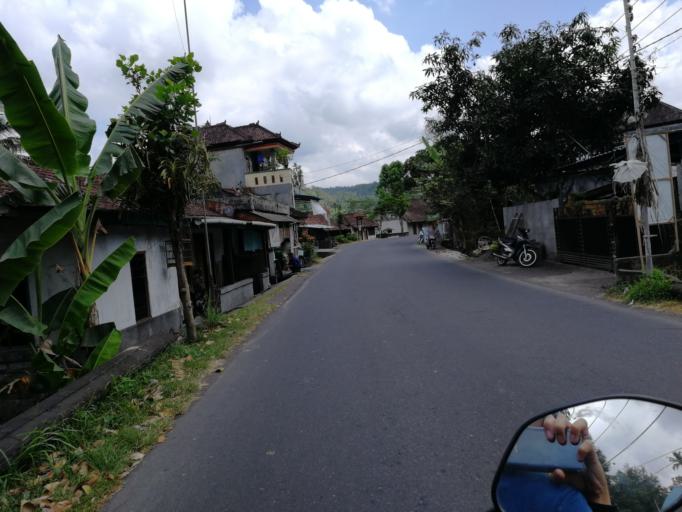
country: ID
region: Bali
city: Banjar Wangsian
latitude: -8.4582
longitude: 115.4500
